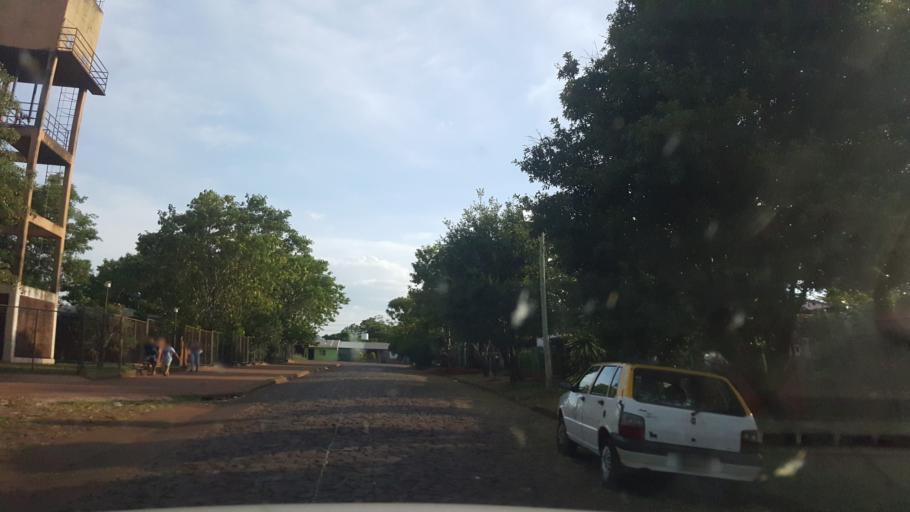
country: AR
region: Misiones
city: Garupa
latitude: -27.4348
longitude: -55.8754
